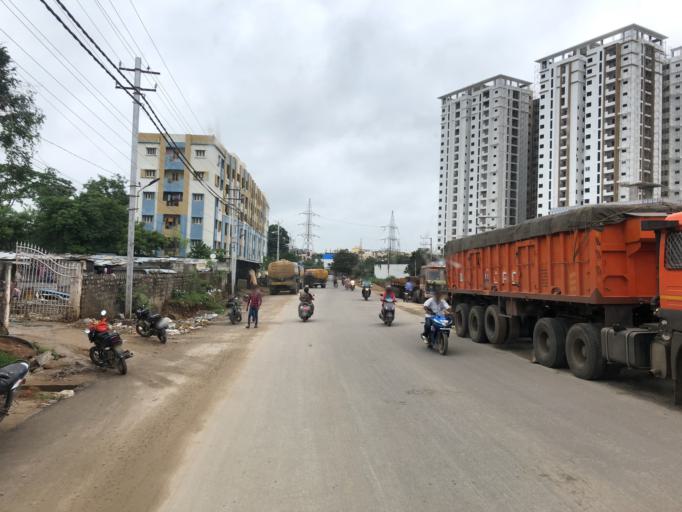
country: IN
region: Telangana
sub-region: Medak
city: Serilingampalle
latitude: 17.4674
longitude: 78.3351
